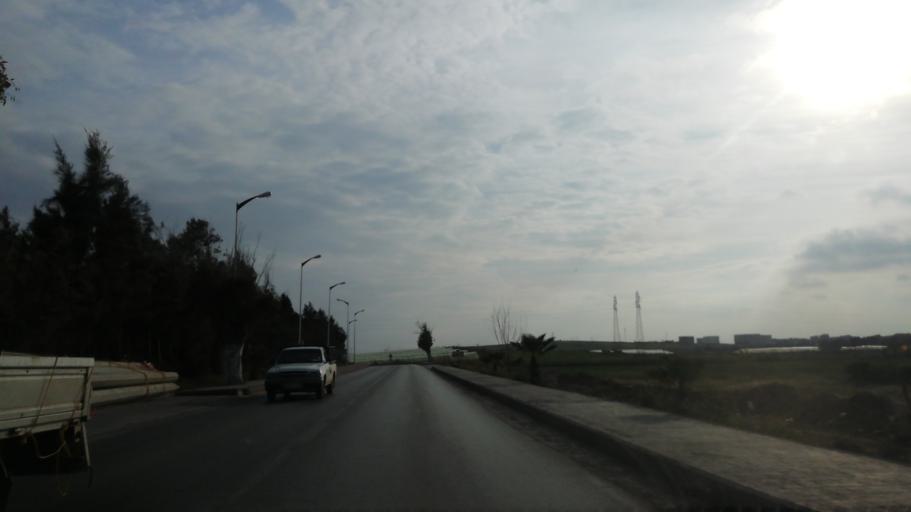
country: DZ
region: Mostaganem
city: Mostaganem
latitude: 35.8908
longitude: 0.0759
